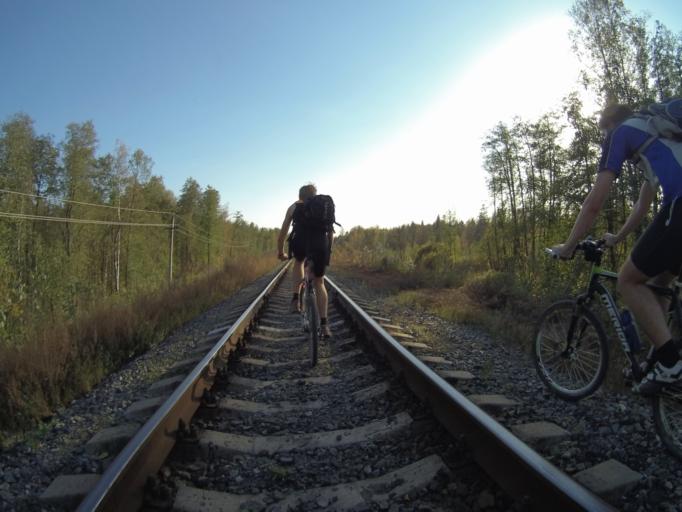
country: RU
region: Vladimir
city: Raduzhnyy
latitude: 56.0395
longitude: 40.3846
